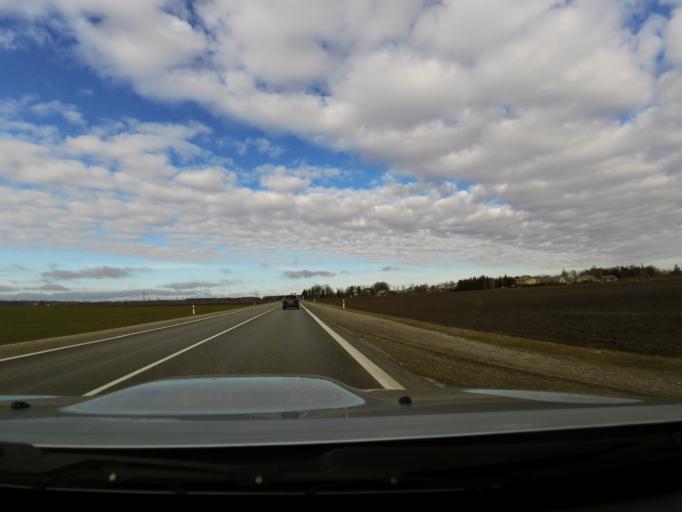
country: LT
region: Panevezys
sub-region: Panevezys City
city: Panevezys
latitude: 55.7617
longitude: 24.0875
